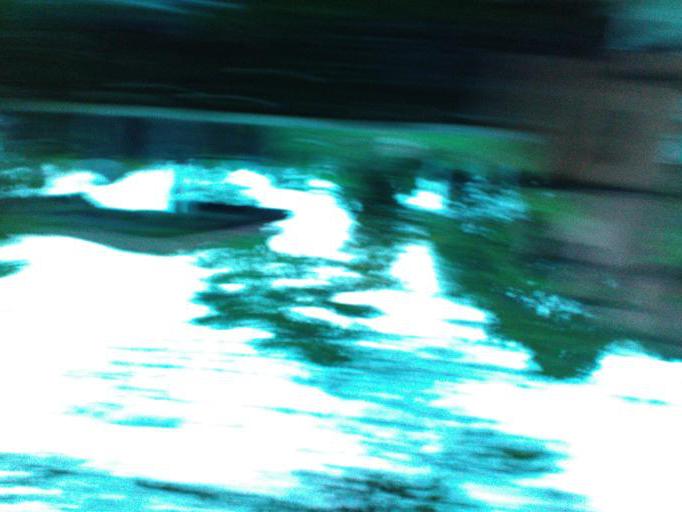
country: ID
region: Central Java
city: Ceper
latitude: -7.6553
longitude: 110.6762
